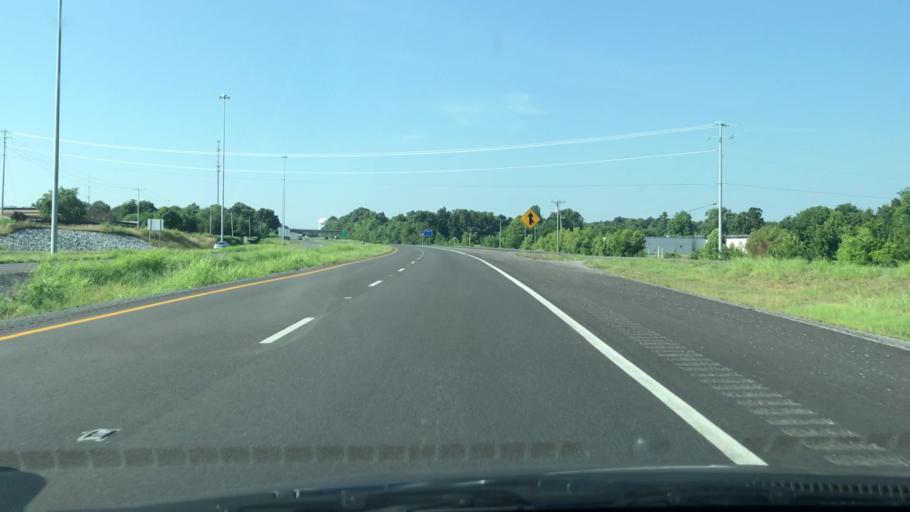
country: US
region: Kentucky
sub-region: Marshall County
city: Benton
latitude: 36.8675
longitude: -88.3660
